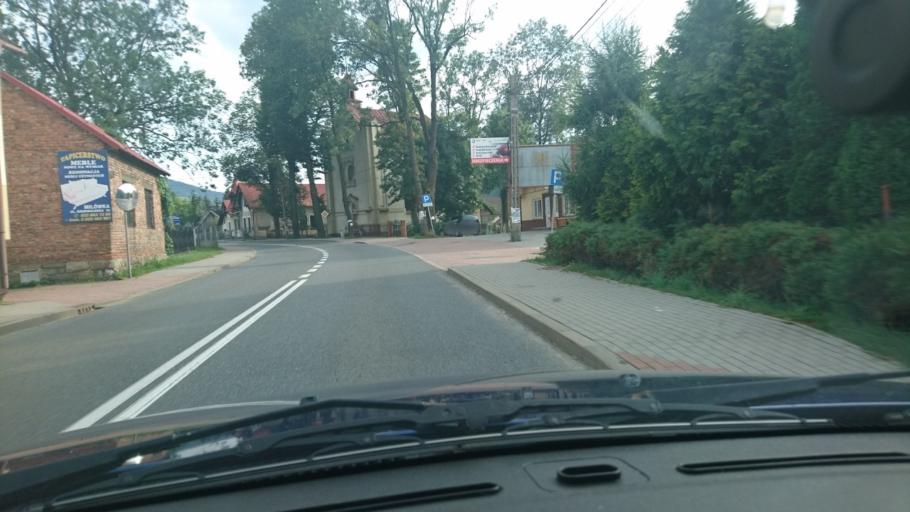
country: PL
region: Silesian Voivodeship
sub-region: Powiat zywiecki
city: Milowka
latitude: 49.5614
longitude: 19.0871
